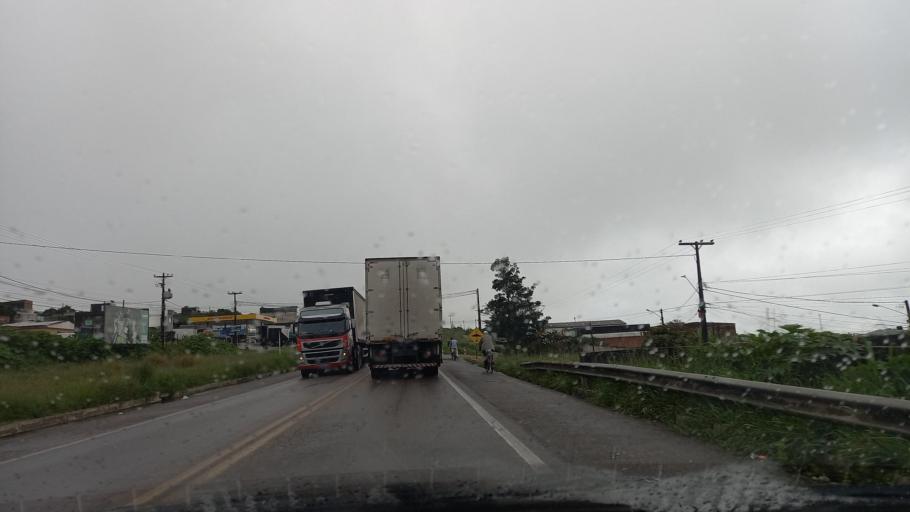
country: BR
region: Pernambuco
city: Garanhuns
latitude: -8.8777
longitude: -36.4988
